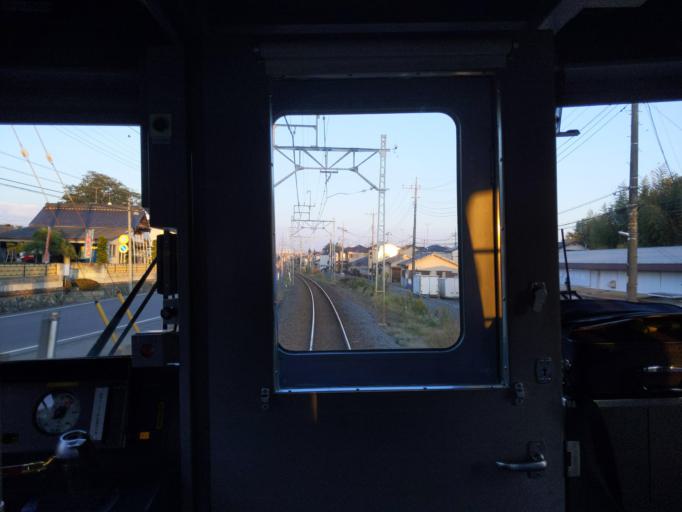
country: JP
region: Saitama
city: Kasukabe
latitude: 35.9796
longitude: 139.8000
